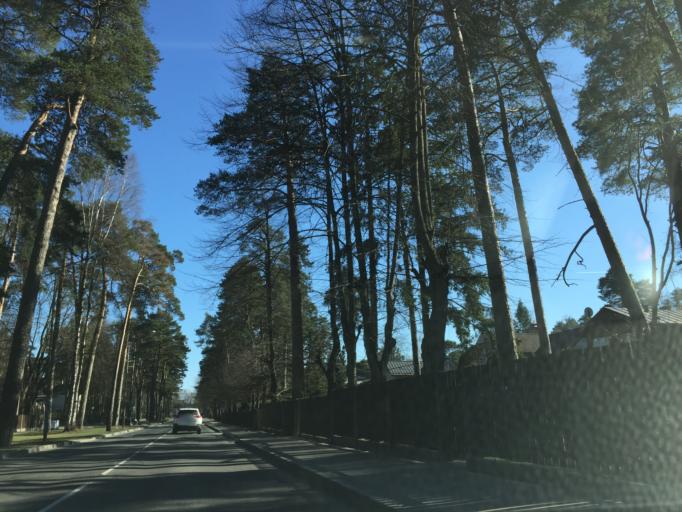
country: LV
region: Babite
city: Pinki
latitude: 56.9799
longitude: 23.8585
